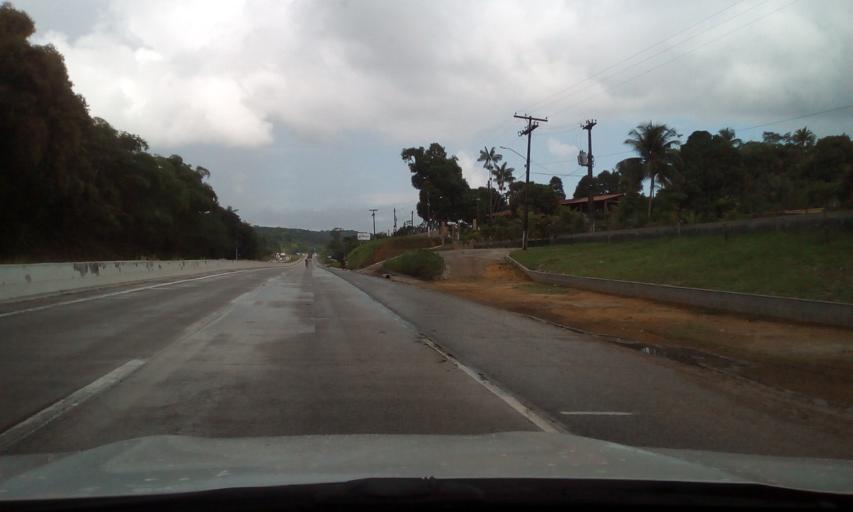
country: BR
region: Pernambuco
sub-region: Cabo De Santo Agostinho
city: Cabo
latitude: -8.3096
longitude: -35.0846
